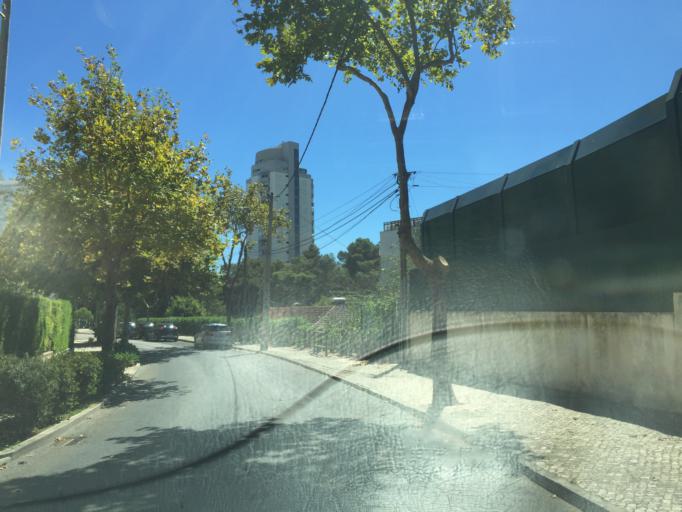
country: PT
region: Lisbon
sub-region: Cascais
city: Cascais
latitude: 38.6986
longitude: -9.4300
